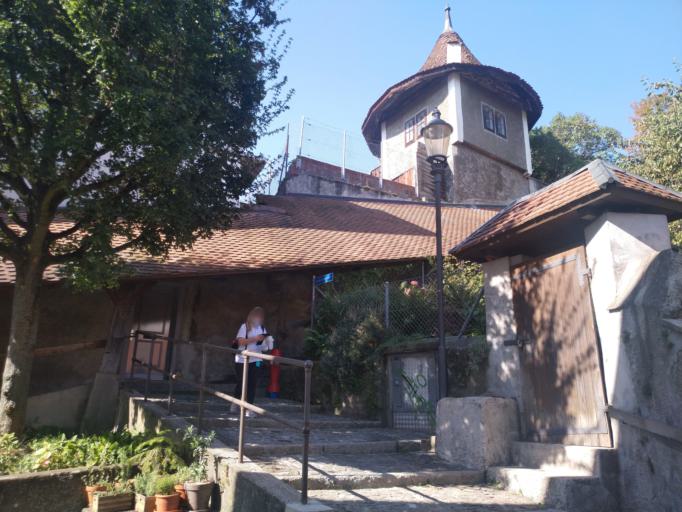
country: CH
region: Fribourg
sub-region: Sarine District
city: Fribourg
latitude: 46.8063
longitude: 7.1595
